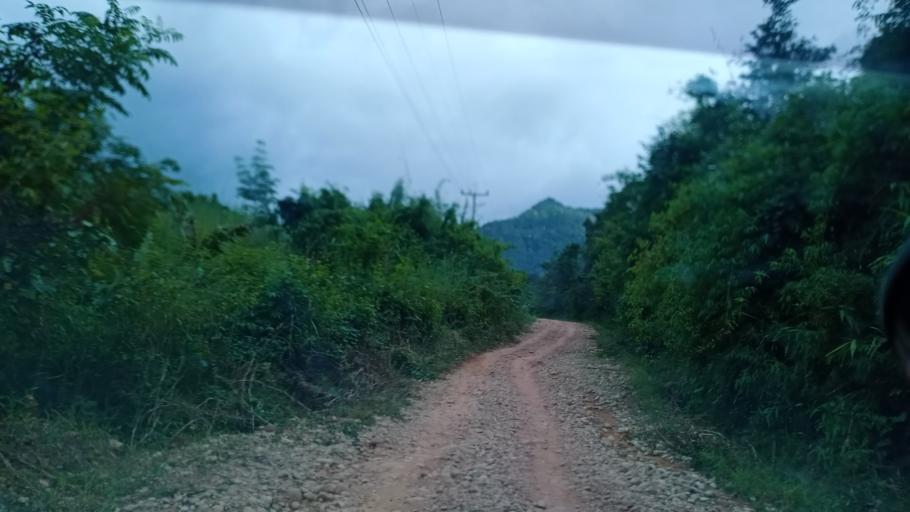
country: TH
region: Changwat Bueng Kan
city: Pak Khat
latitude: 18.7223
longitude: 103.2479
